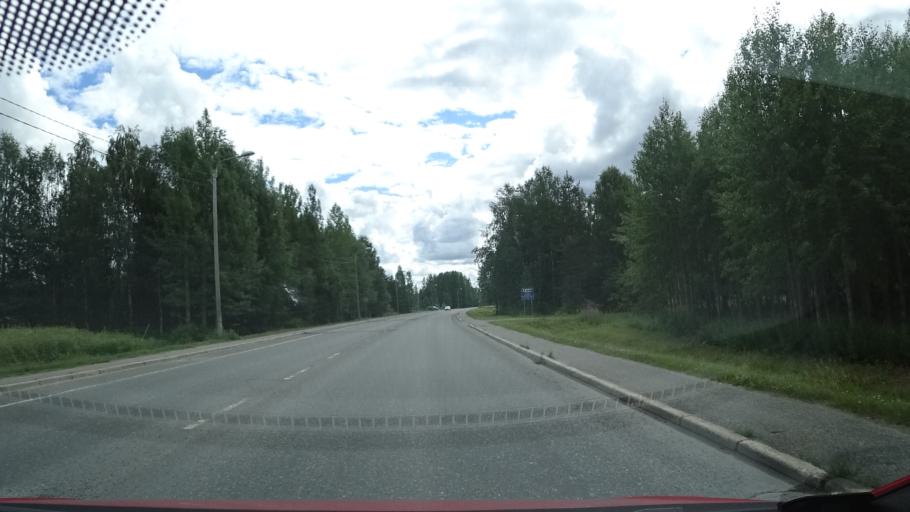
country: FI
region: Lapland
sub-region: Tunturi-Lappi
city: Kittilae
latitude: 67.6485
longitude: 24.9186
